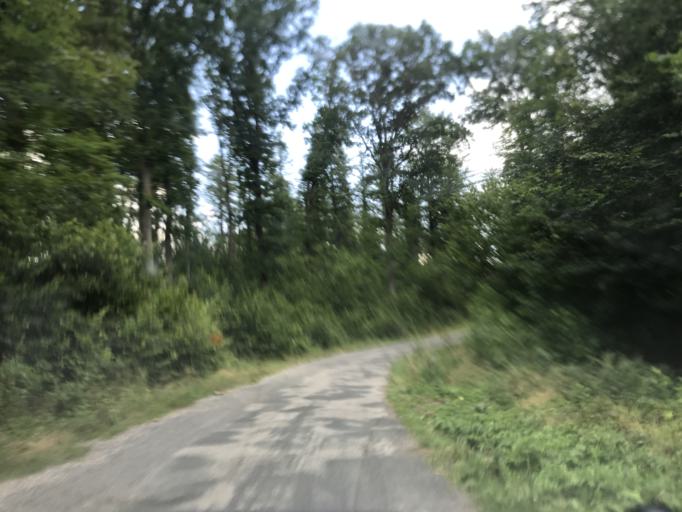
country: PL
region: West Pomeranian Voivodeship
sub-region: Powiat lobeski
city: Wegorzyno
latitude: 53.5048
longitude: 15.4927
